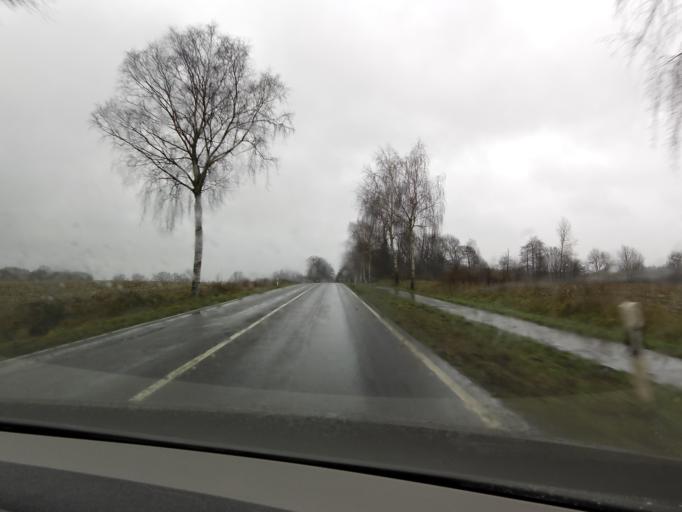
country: DE
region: Lower Saxony
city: Bad Fallingbostel
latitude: 52.8871
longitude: 9.7438
